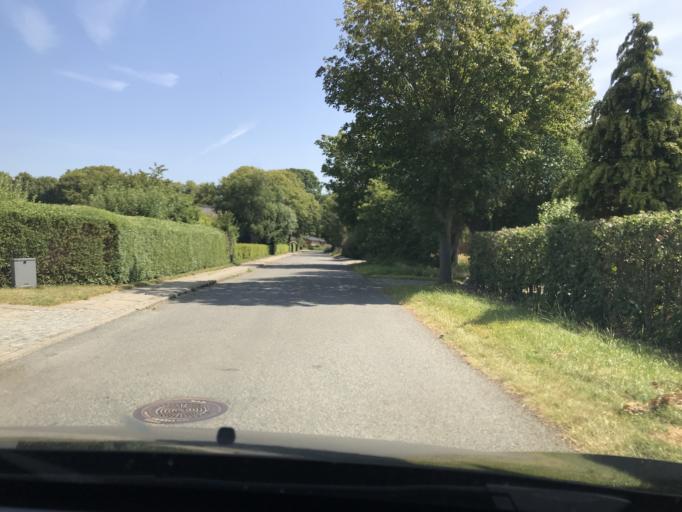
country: DK
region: South Denmark
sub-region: AEro Kommune
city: AEroskobing
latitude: 54.8880
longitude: 10.4029
